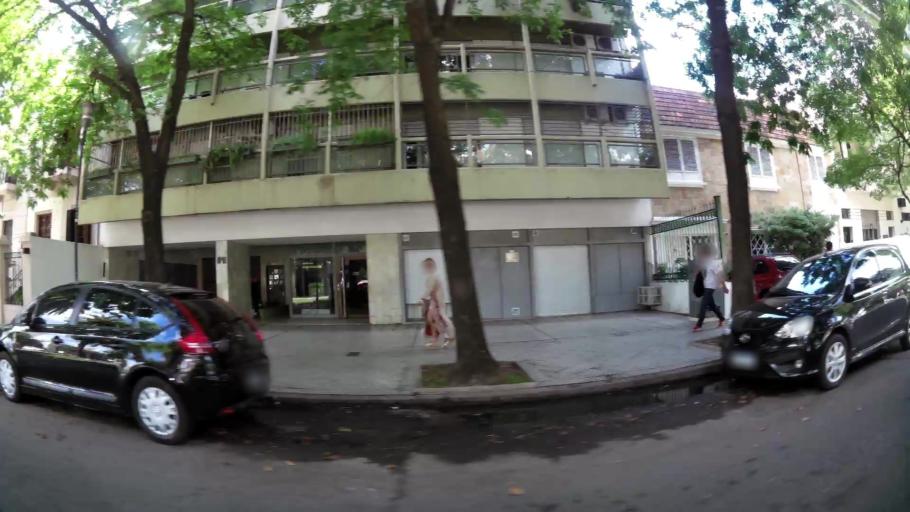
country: AR
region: Santa Fe
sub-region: Departamento de Rosario
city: Rosario
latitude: -32.9383
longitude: -60.6518
